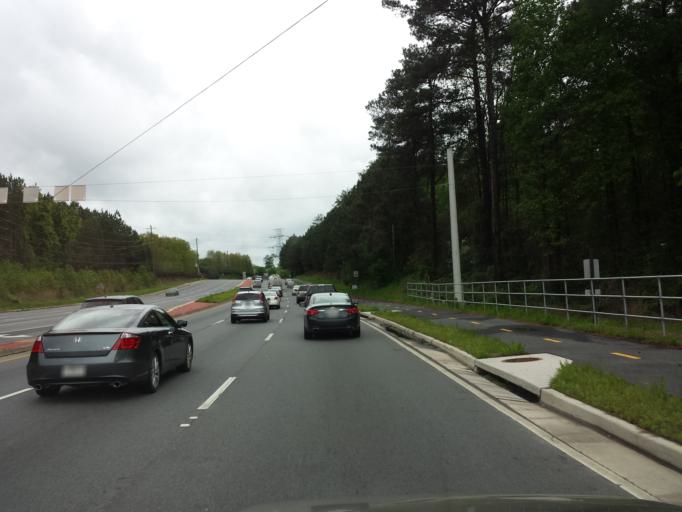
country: US
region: Georgia
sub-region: Cobb County
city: Kennesaw
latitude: 33.9982
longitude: -84.5880
